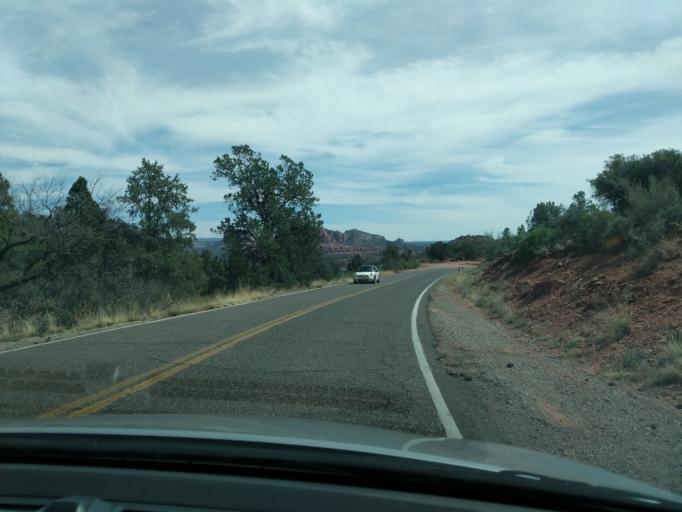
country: US
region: Arizona
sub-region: Yavapai County
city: West Sedona
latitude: 34.8441
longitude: -111.8266
